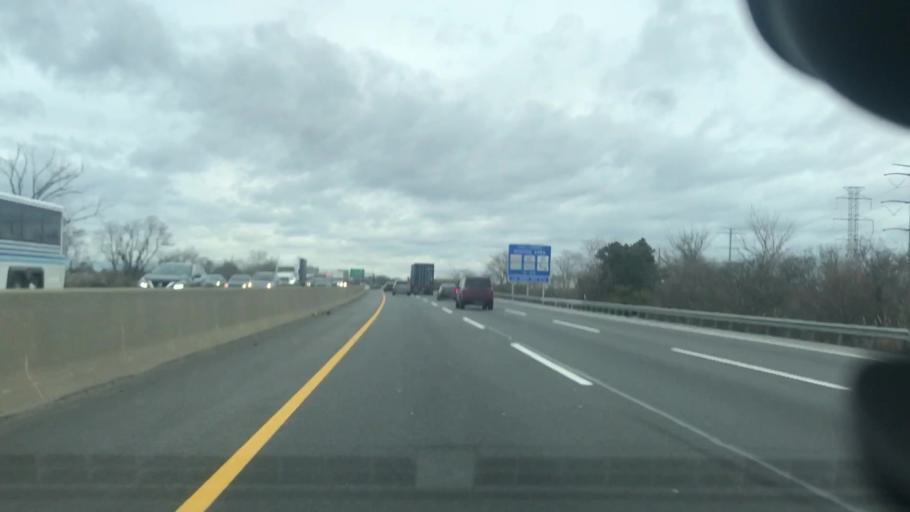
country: US
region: New Jersey
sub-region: Hudson County
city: North Bergen
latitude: 40.8114
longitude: -74.0294
